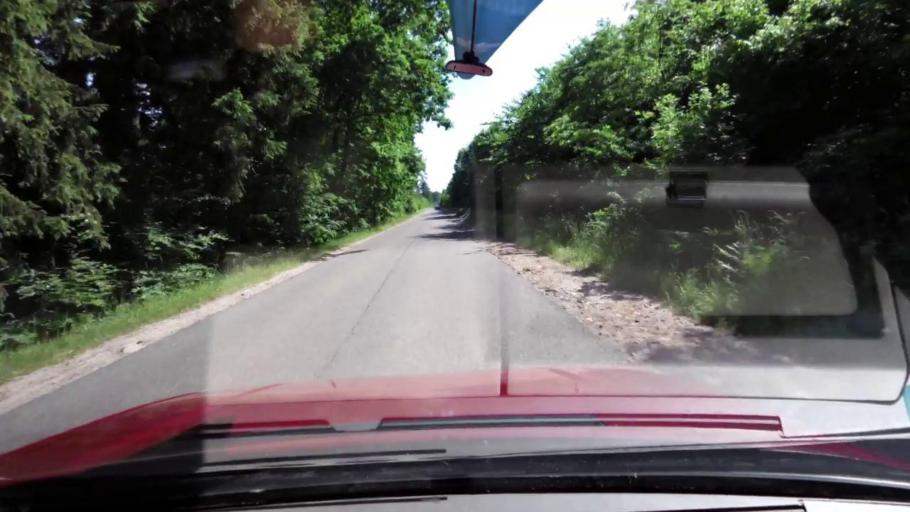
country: PL
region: Pomeranian Voivodeship
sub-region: Powiat slupski
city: Kepice
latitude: 54.3272
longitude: 16.9620
